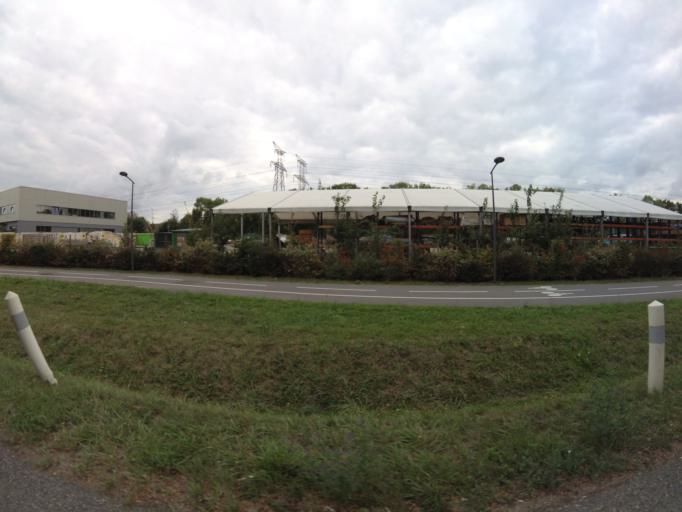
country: FR
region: Ile-de-France
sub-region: Departement de Seine-et-Marne
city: Torcy
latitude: 48.8476
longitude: 2.6634
